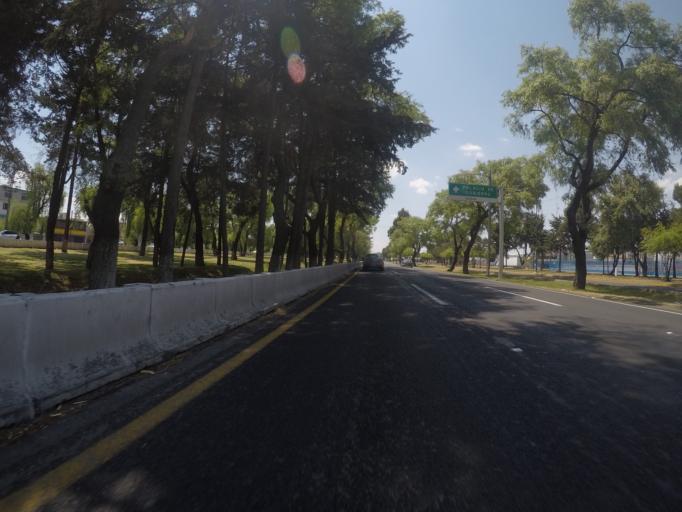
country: MX
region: Mexico
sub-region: Lerma
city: Colonia Isidro Fabela
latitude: 19.2858
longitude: -99.5314
